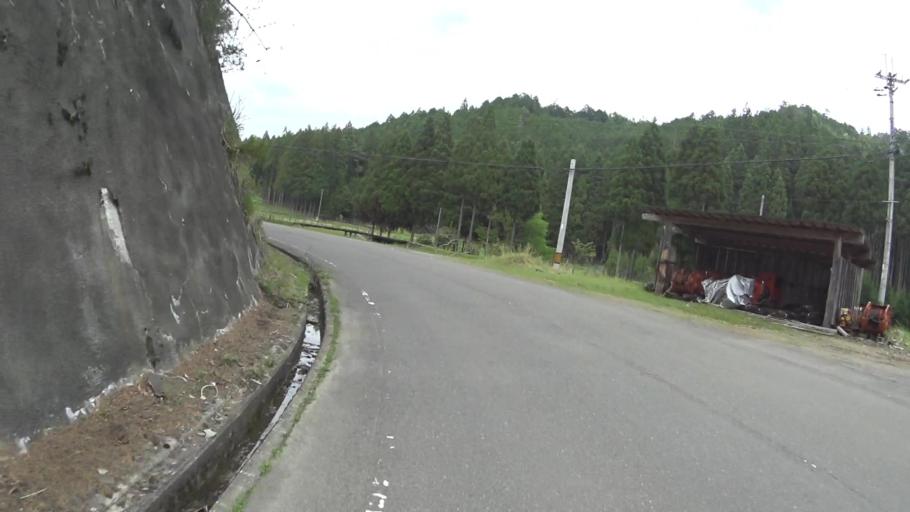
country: JP
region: Kyoto
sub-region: Kyoto-shi
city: Kamigyo-ku
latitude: 35.1996
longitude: 135.6982
